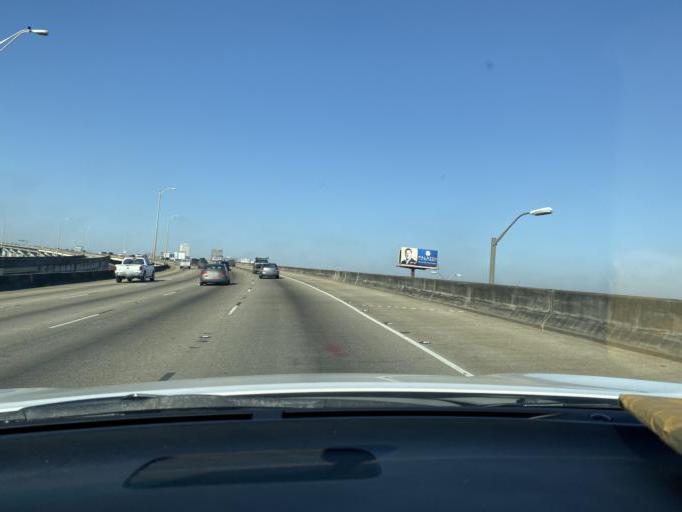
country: US
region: Louisiana
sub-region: Jefferson Parish
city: Gretna
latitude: 29.9376
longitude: -90.0394
